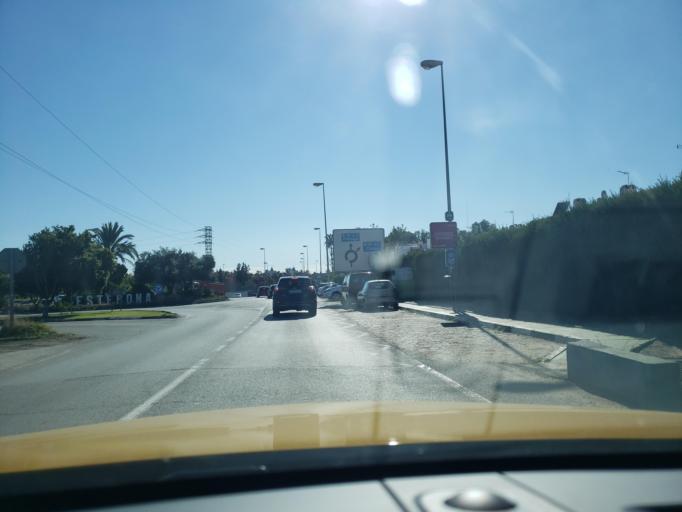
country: ES
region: Andalusia
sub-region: Provincia de Malaga
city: Benahavis
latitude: 36.4736
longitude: -5.0119
